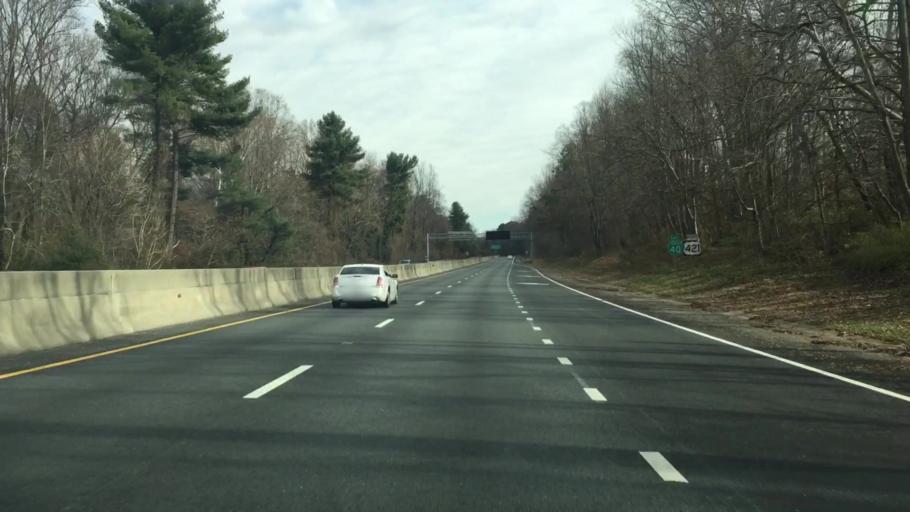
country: US
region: North Carolina
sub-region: Forsyth County
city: Winston-Salem
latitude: 36.0877
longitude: -80.2987
